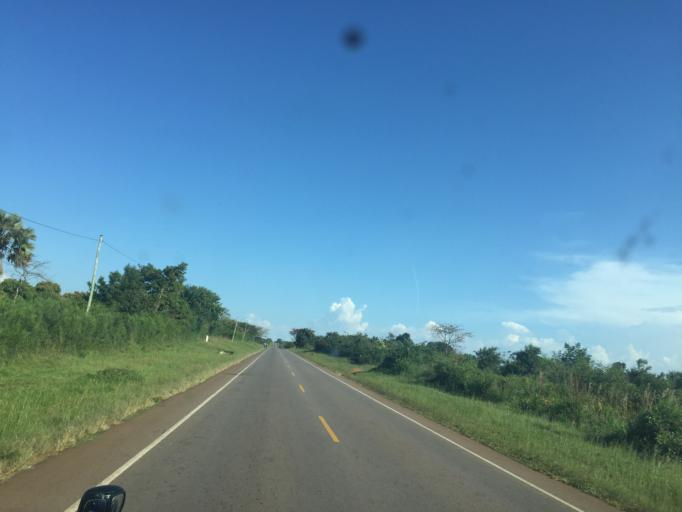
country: UG
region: Central Region
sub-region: Nakasongola District
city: Nakasongola
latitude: 1.3509
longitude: 32.3824
